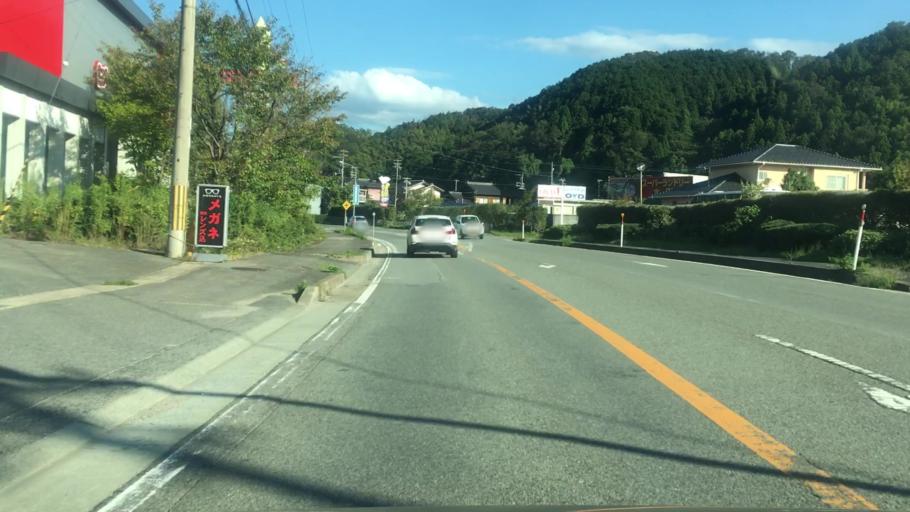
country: JP
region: Hyogo
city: Toyooka
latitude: 35.5550
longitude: 134.8343
